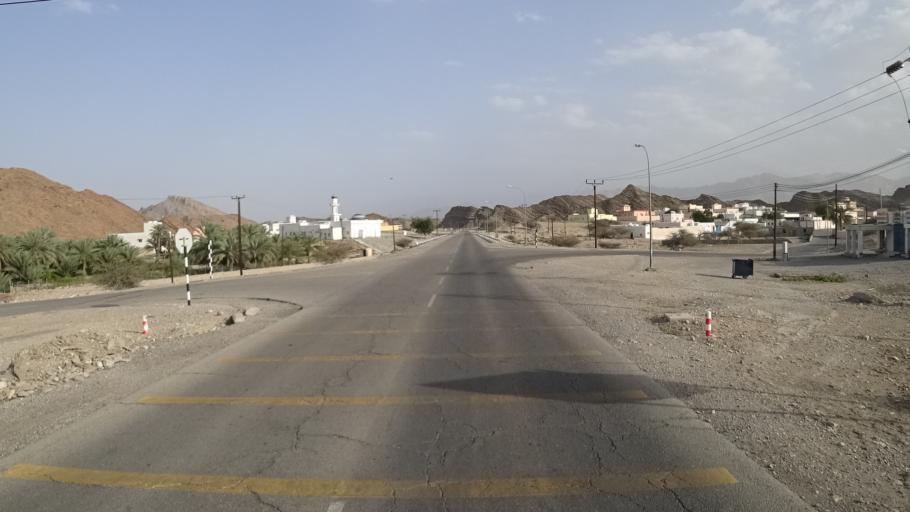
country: OM
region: Muhafazat Masqat
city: Bawshar
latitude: 23.3763
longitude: 58.5153
